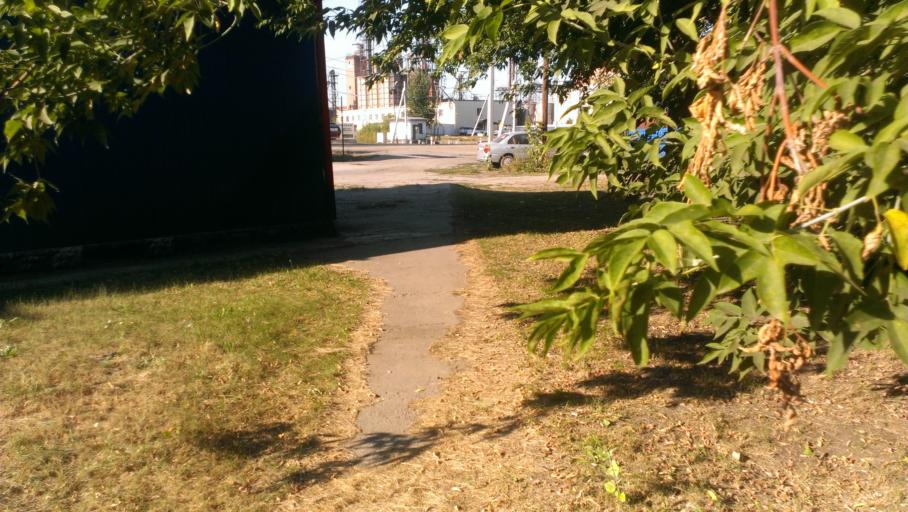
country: RU
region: Altai Krai
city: Novosilikatnyy
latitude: 53.3108
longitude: 83.6210
